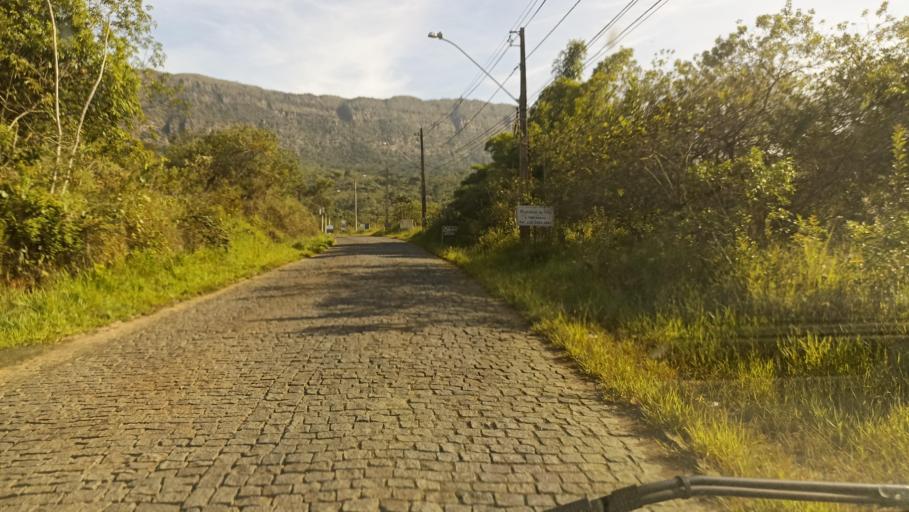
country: BR
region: Minas Gerais
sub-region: Tiradentes
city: Tiradentes
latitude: -21.1172
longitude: -44.1896
